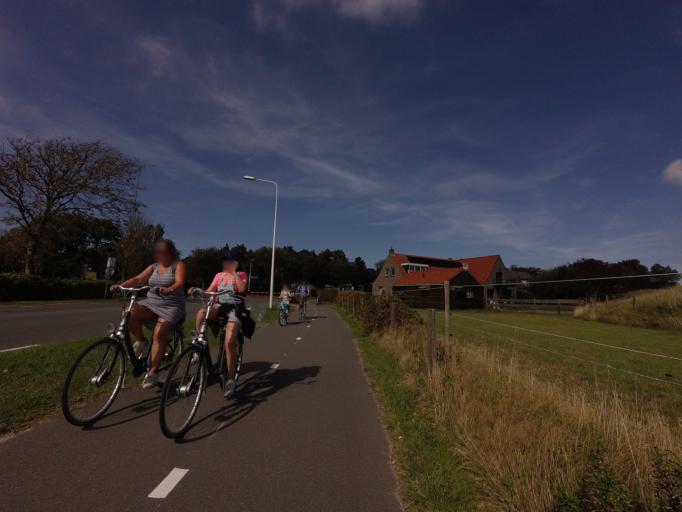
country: NL
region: Friesland
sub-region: Gemeente Ameland
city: Nes
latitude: 53.4454
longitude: 5.7648
